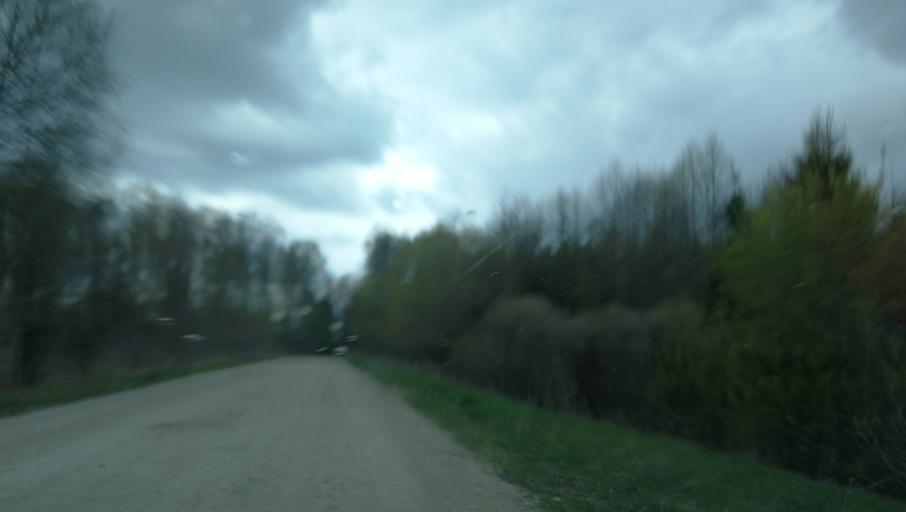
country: LV
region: Babite
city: Pinki
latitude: 56.9839
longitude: 23.9608
